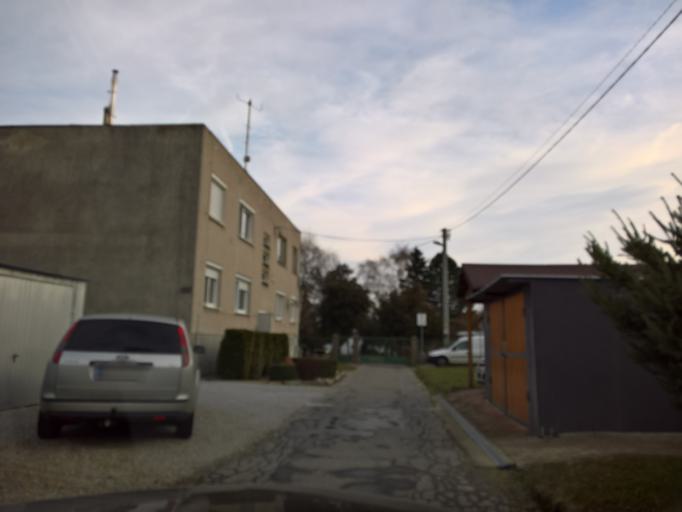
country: SK
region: Nitriansky
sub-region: Okres Nitra
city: Nitra
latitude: 48.3783
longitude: 18.1676
